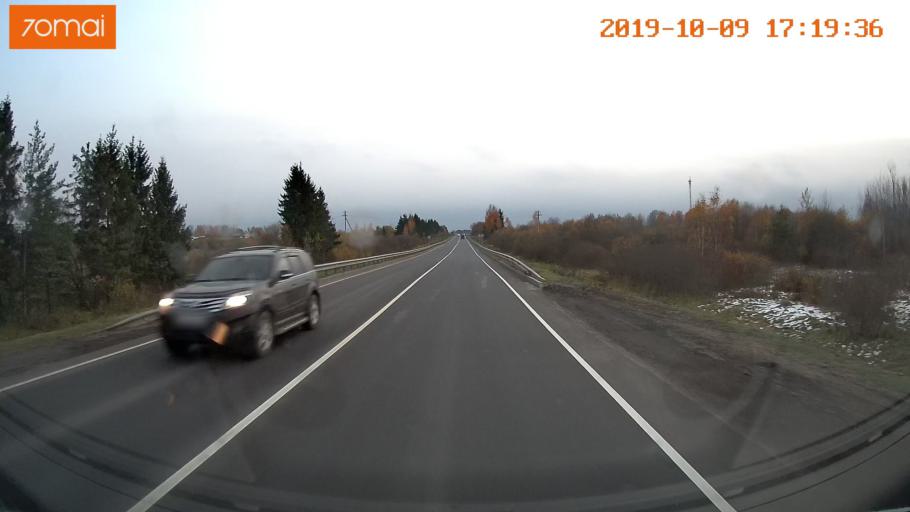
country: RU
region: Ivanovo
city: Furmanov
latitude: 57.2442
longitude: 41.1509
